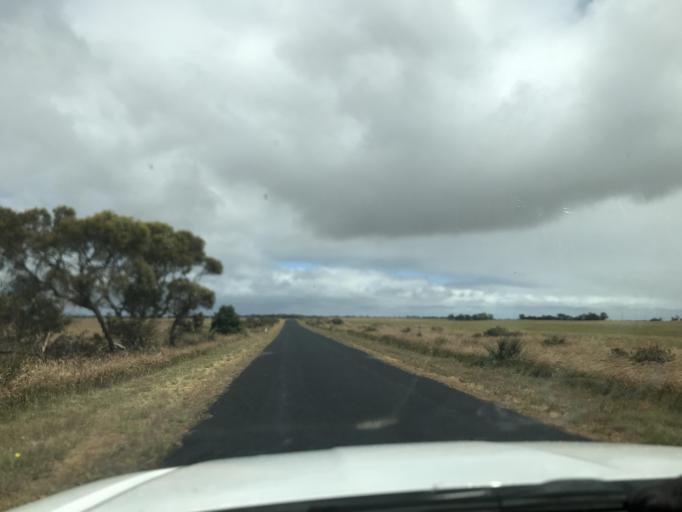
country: AU
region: South Australia
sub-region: Tatiara
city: Bordertown
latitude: -36.1353
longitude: 141.1840
